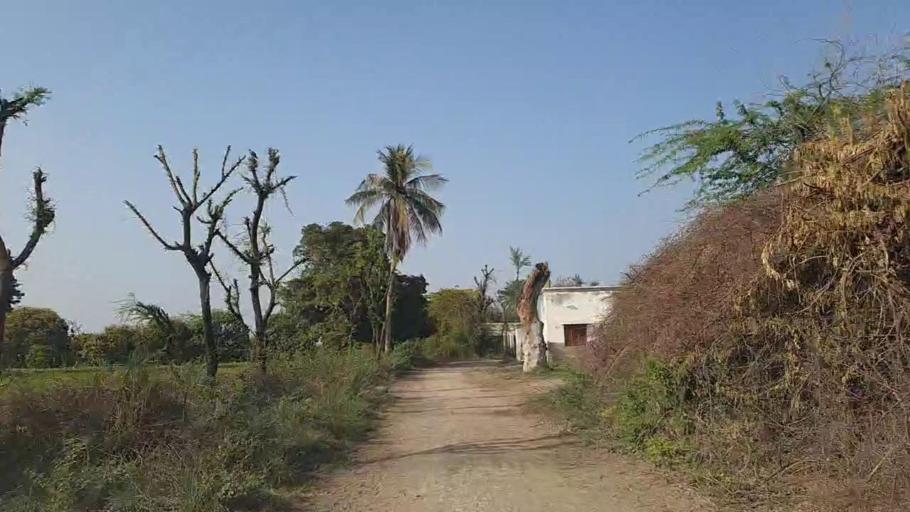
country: PK
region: Sindh
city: Dhoro Naro
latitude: 25.5103
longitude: 69.5345
